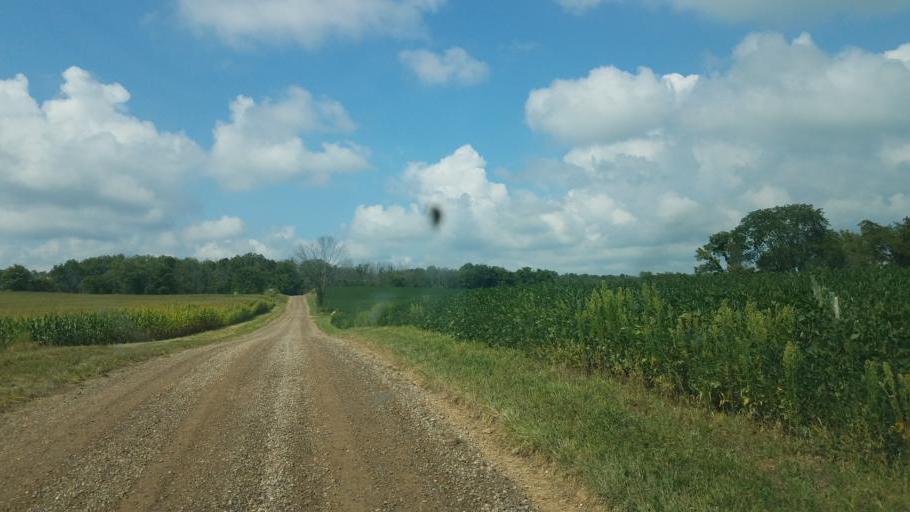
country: US
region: Ohio
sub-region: Licking County
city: Utica
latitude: 40.2530
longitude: -82.4171
